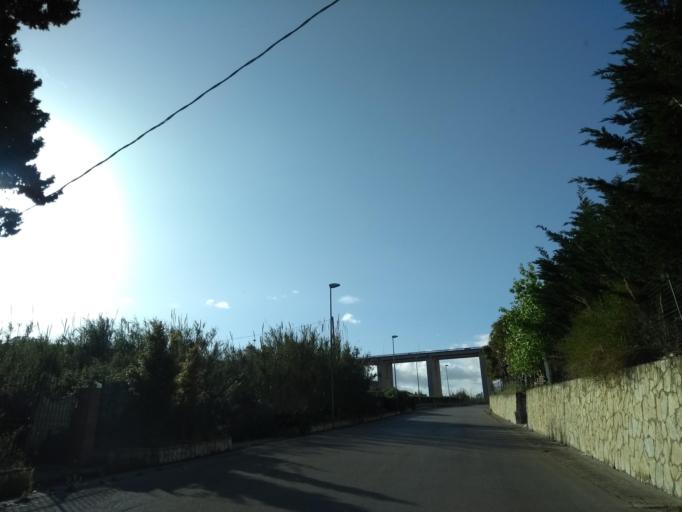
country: IT
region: Sicily
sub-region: Trapani
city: Alcamo
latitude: 38.0178
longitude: 12.9507
